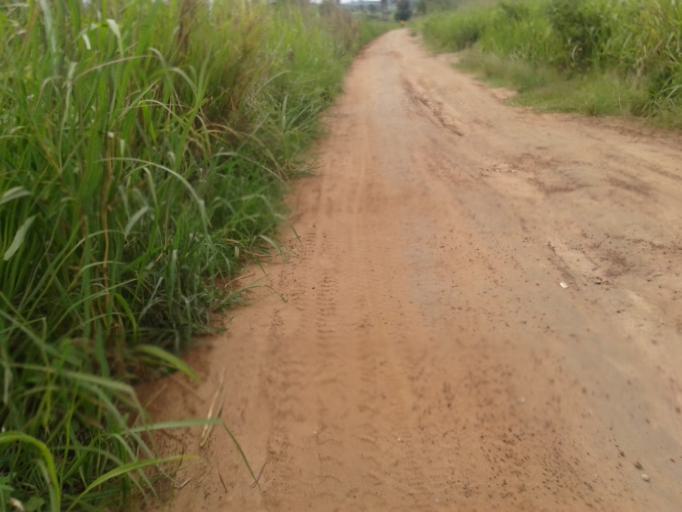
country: UG
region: Northern Region
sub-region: Gulu District
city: Gulu
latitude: 2.8276
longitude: 32.2557
